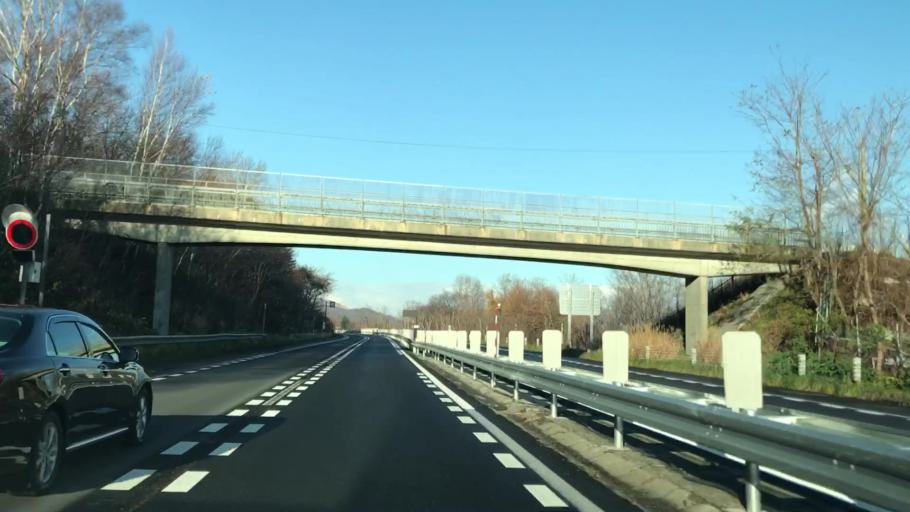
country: JP
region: Hokkaido
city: Otaru
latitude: 43.1342
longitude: 141.1710
